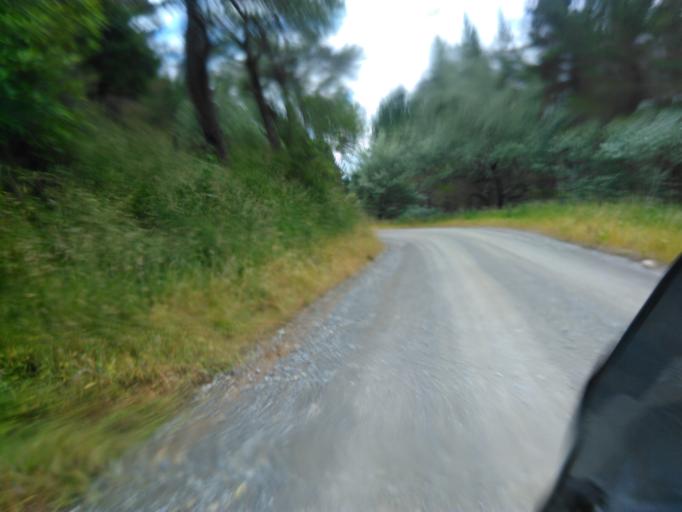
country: NZ
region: Gisborne
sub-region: Gisborne District
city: Gisborne
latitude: -38.0593
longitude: 178.1544
